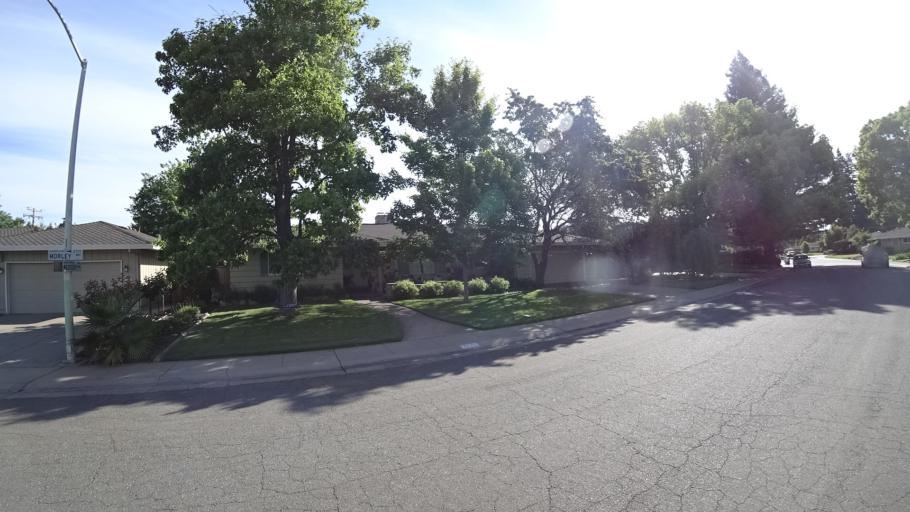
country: US
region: California
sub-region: Sacramento County
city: Rosemont
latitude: 38.5666
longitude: -121.3992
